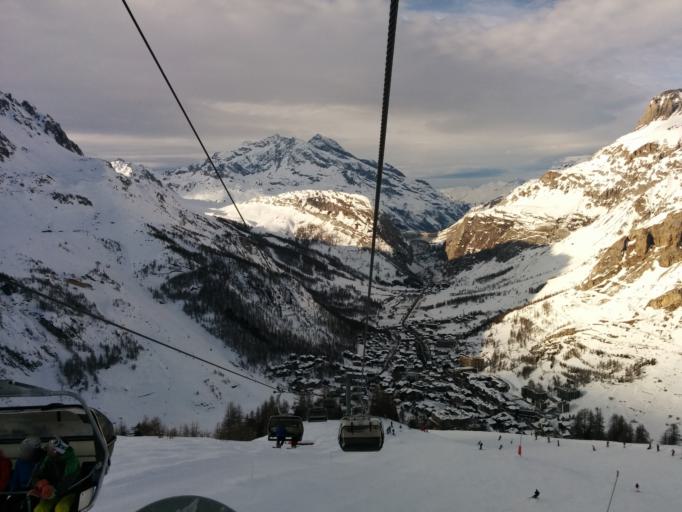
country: FR
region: Rhone-Alpes
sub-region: Departement de la Savoie
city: Val-d'Isere
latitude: 45.4392
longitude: 6.9871
